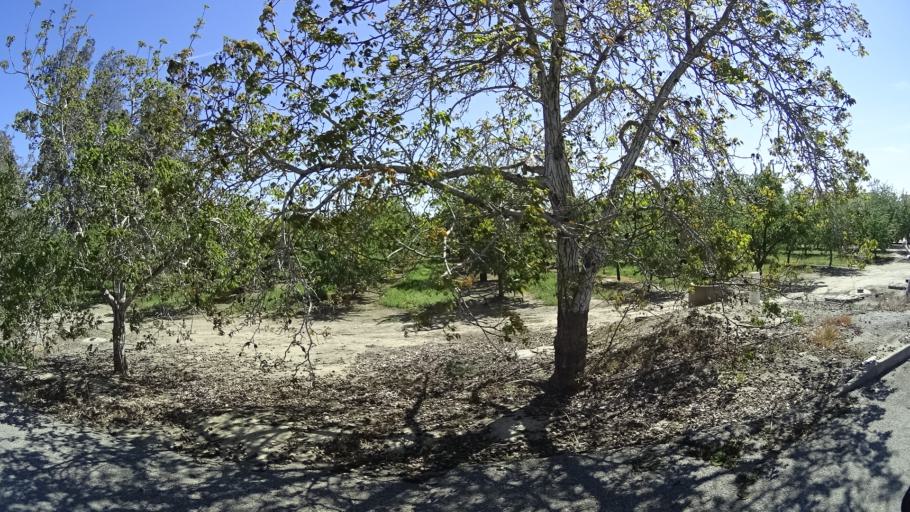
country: US
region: California
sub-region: Glenn County
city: Orland
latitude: 39.7452
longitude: -122.1275
